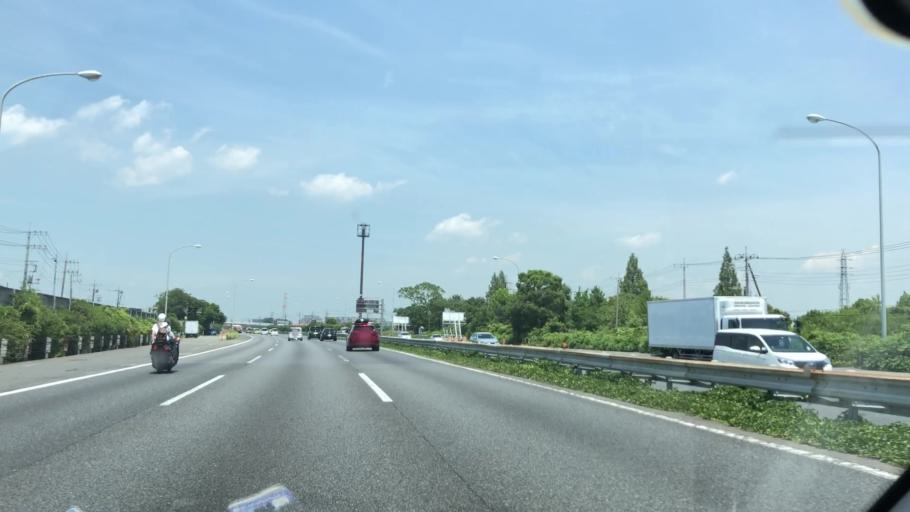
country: JP
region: Saitama
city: Shiraoka
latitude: 36.0180
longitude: 139.6750
